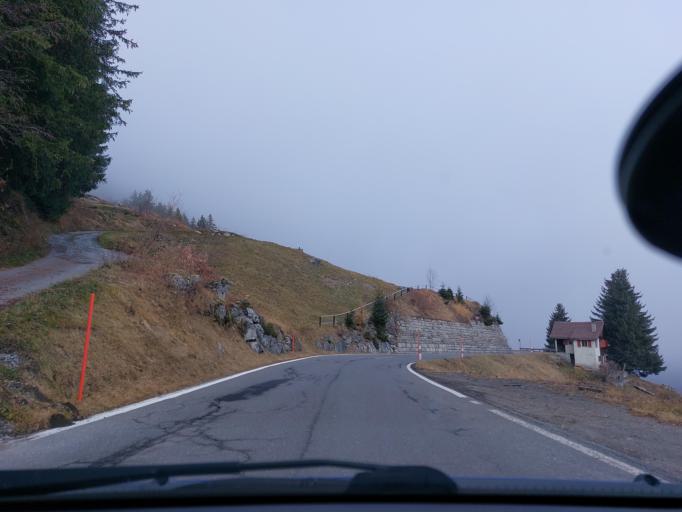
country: CH
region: Valais
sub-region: Conthey District
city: Basse-Nendaz
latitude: 46.1538
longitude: 7.3147
